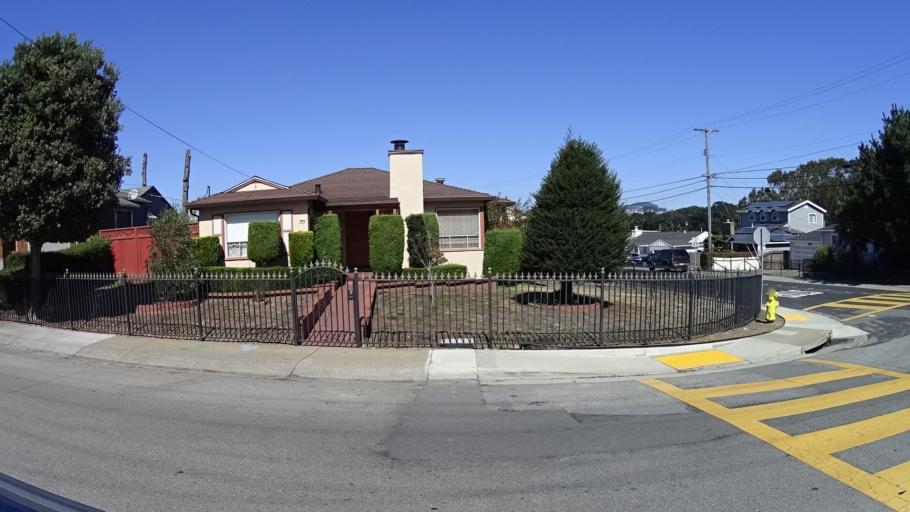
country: US
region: California
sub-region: San Mateo County
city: Broadmoor
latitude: 37.6932
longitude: -122.4818
